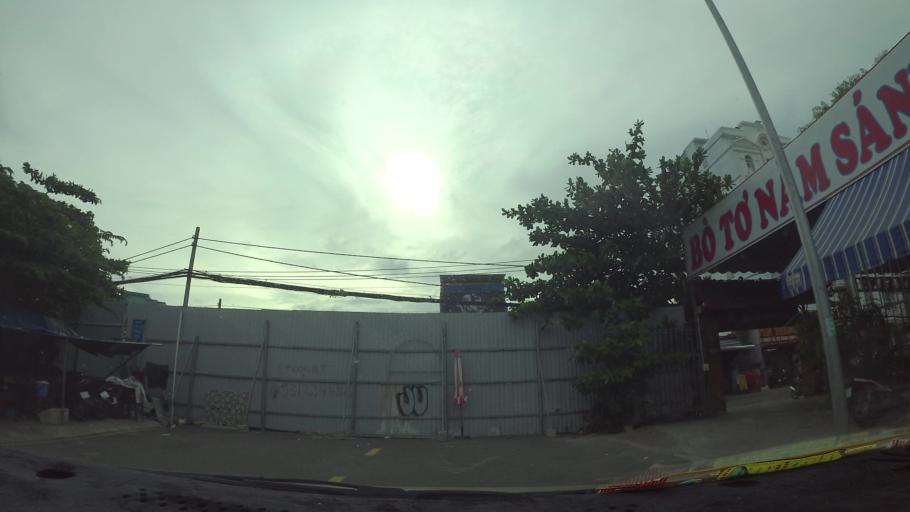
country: VN
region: Ho Chi Minh City
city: Quan Sau
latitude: 10.7450
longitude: 106.6534
